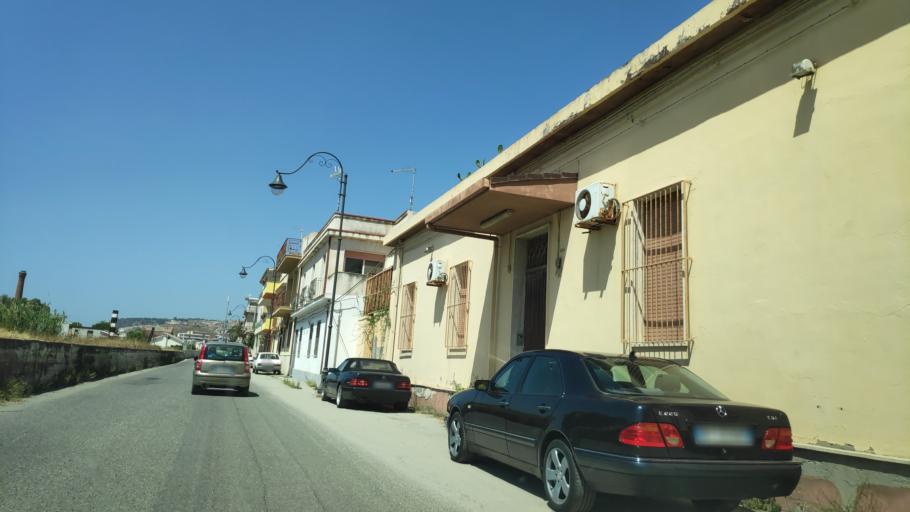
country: IT
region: Calabria
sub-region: Provincia di Reggio Calabria
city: Bova Marina
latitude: 37.9296
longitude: 15.9287
